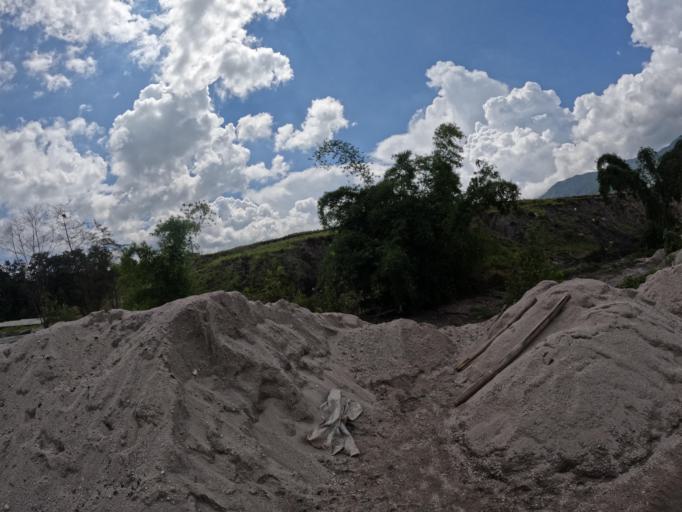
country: NP
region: Central Region
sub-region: Bagmati Zone
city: Kathmandu
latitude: 27.7811
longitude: 85.3274
